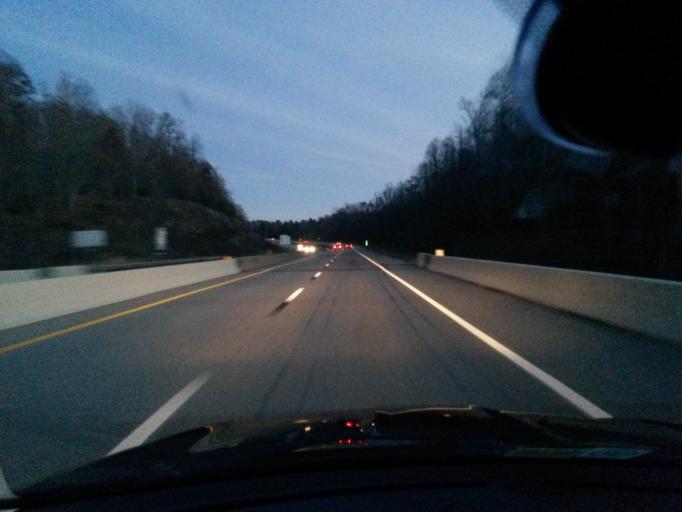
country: US
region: West Virginia
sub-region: Raleigh County
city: Shady Spring
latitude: 37.7669
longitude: -81.0373
